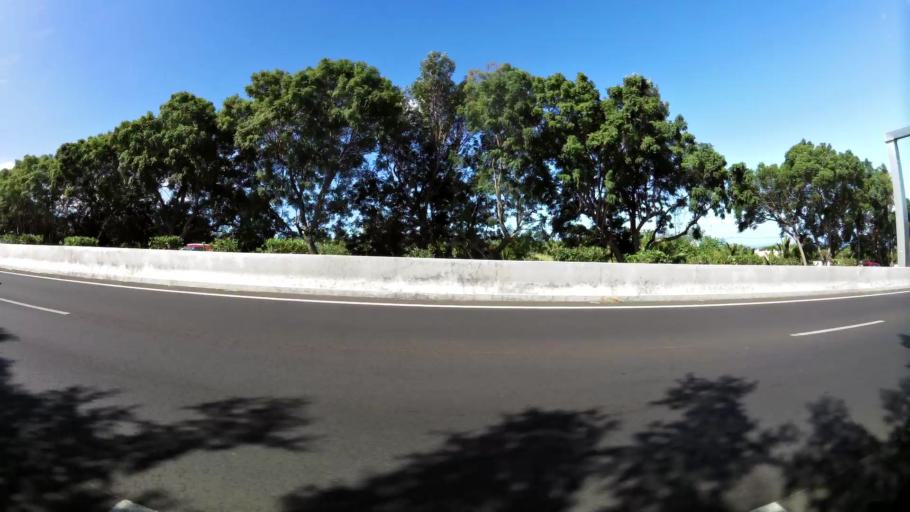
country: RE
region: Reunion
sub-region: Reunion
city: Le Tampon
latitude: -21.2932
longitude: 55.5118
